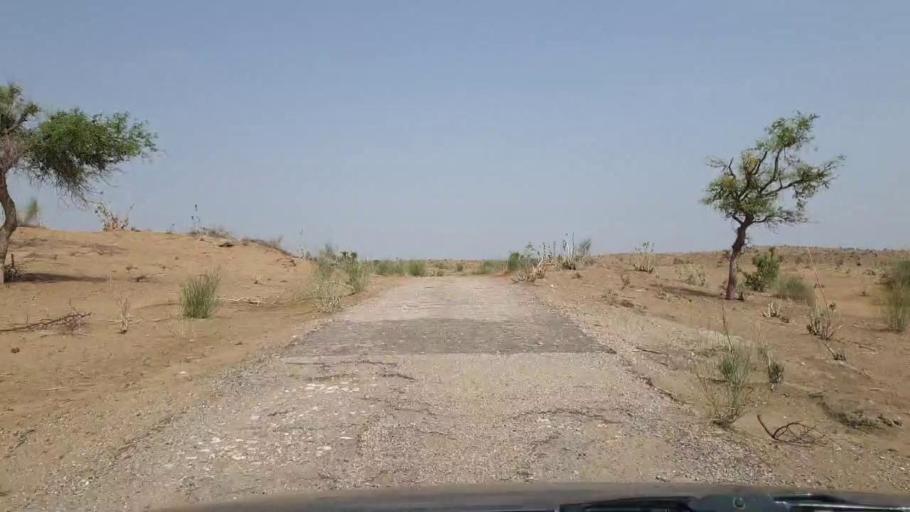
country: PK
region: Sindh
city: Chor
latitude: 25.4695
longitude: 70.5210
